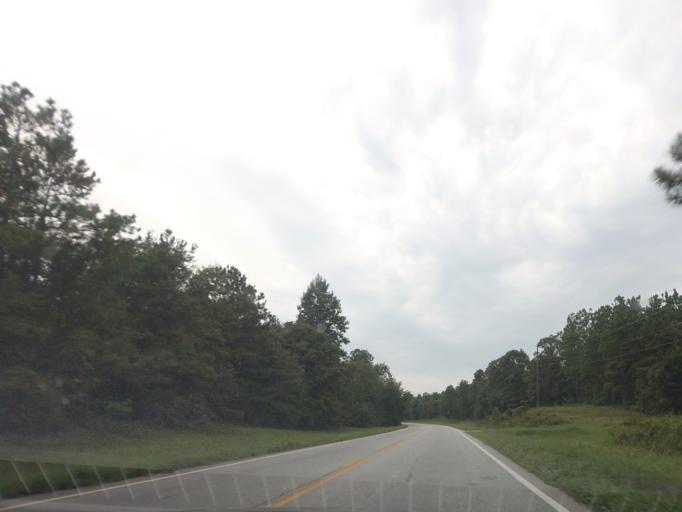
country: US
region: Georgia
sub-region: Twiggs County
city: Jeffersonville
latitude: 32.7633
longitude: -83.4624
